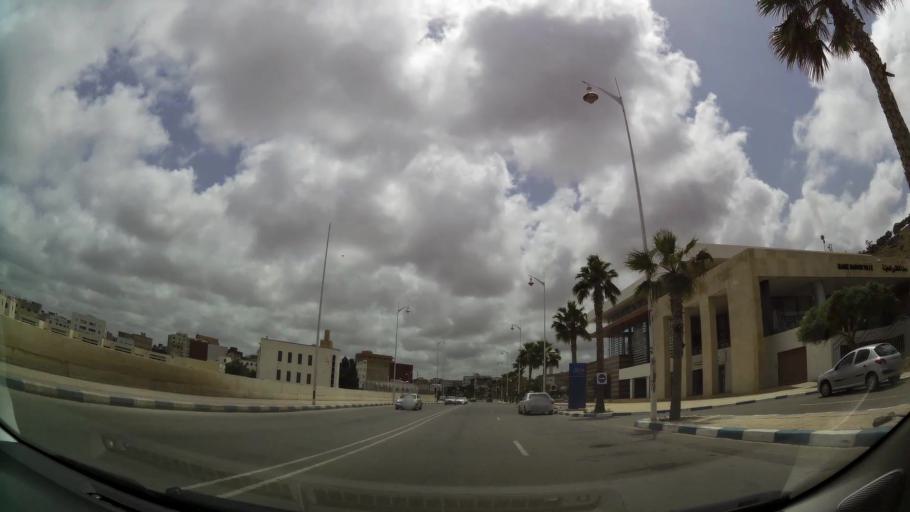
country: MA
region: Oriental
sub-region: Nador
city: Nador
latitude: 35.1848
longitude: -2.9275
